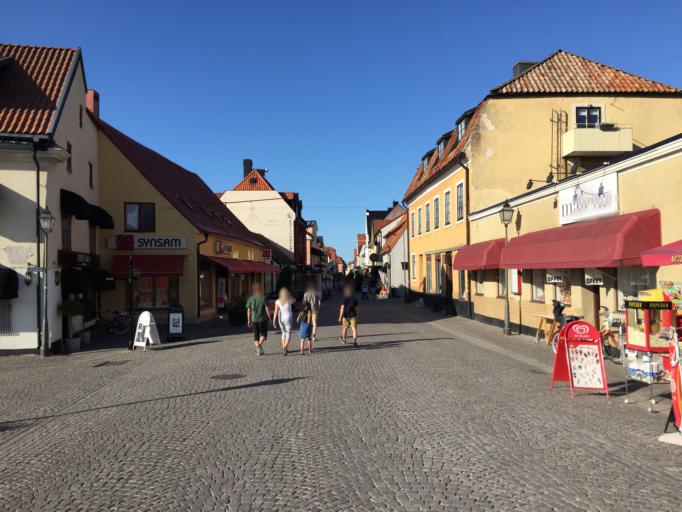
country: SE
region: Gotland
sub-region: Gotland
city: Visby
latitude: 57.6351
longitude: 18.2921
